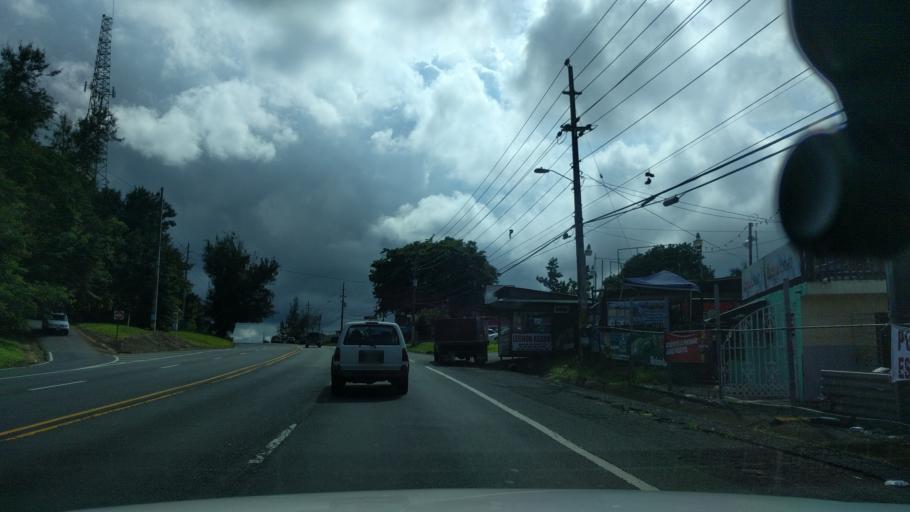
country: PR
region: Toa Alta
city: Pajaros
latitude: 18.3586
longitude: -66.1905
